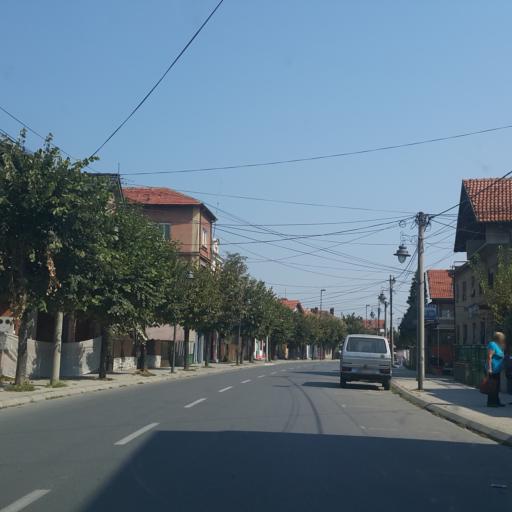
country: RS
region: Central Serbia
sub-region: Zajecarski Okrug
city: Zajecar
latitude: 43.9057
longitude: 22.2842
